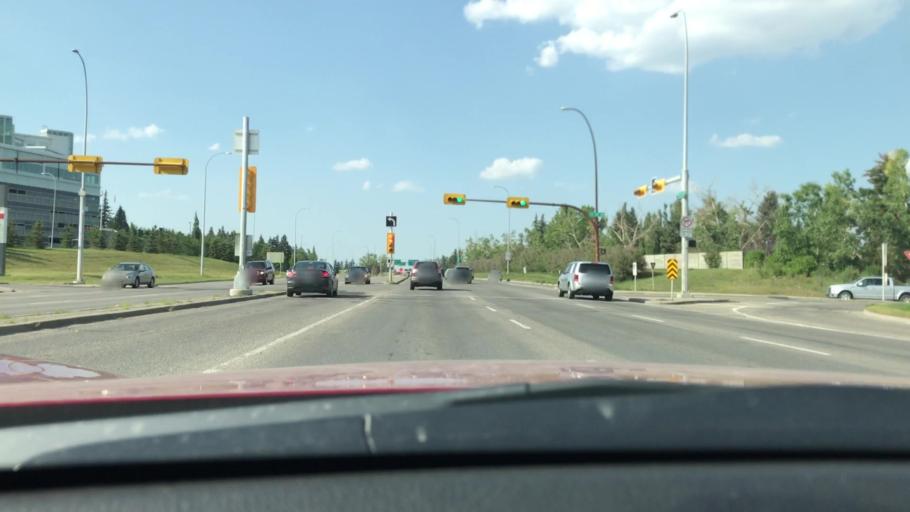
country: CA
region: Alberta
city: Calgary
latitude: 50.9878
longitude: -114.0948
